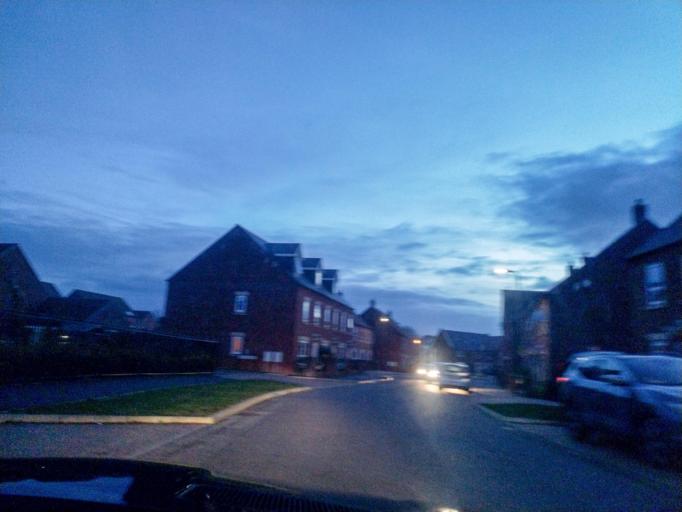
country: GB
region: England
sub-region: Oxfordshire
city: Adderbury
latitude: 52.0391
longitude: -1.3196
